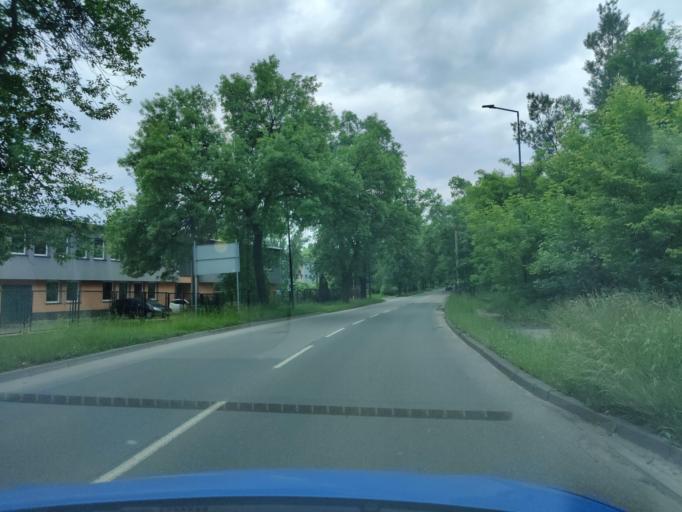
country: PL
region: Silesian Voivodeship
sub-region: Myslowice
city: Myslowice
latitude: 50.2557
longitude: 19.1503
